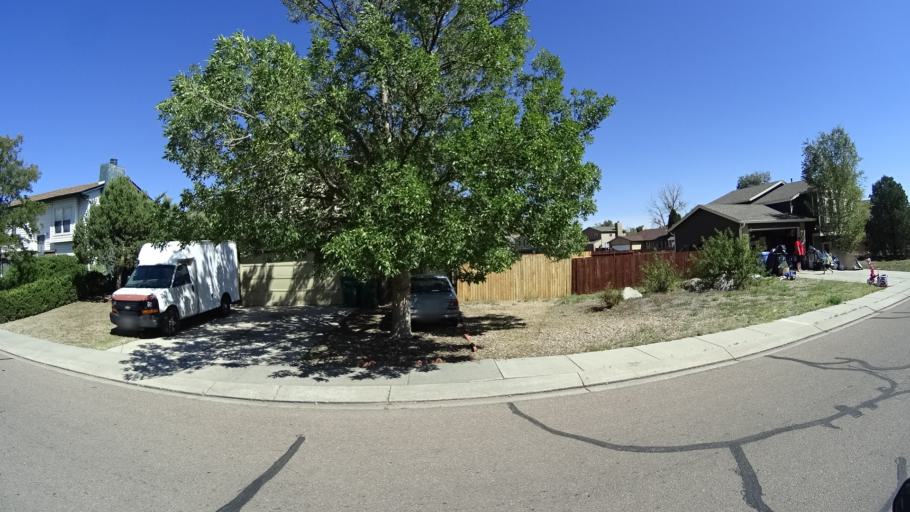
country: US
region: Colorado
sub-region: El Paso County
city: Stratmoor
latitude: 38.7868
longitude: -104.7524
